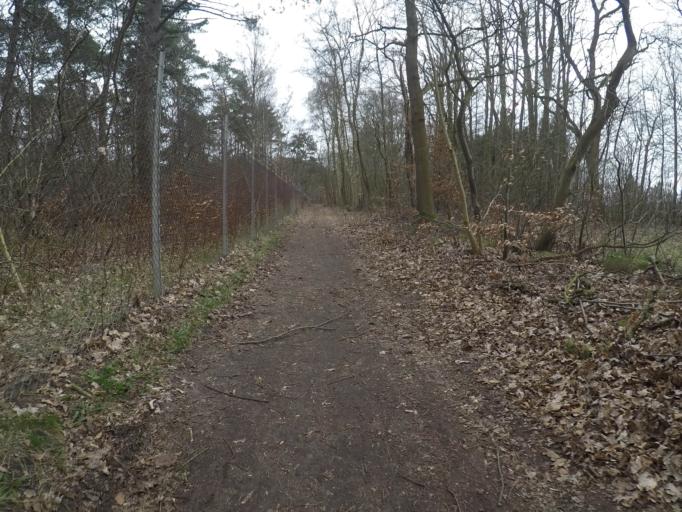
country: DE
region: Lower Saxony
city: Nordholz
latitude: 53.8024
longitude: 8.6239
